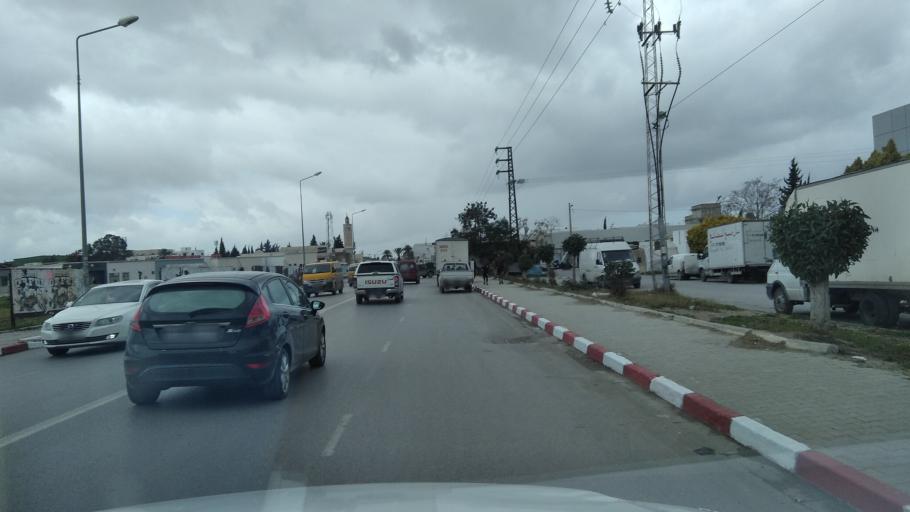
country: TN
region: Bin 'Arus
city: Ben Arous
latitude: 36.7495
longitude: 10.2278
